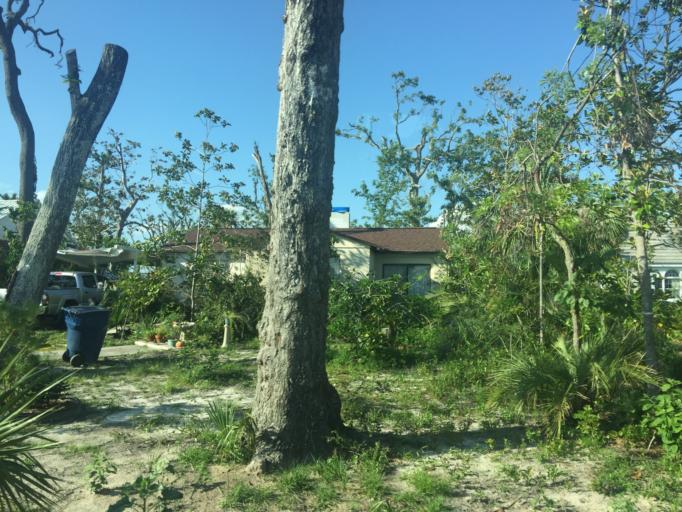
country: US
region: Florida
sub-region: Bay County
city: Panama City
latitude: 30.1438
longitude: -85.6500
